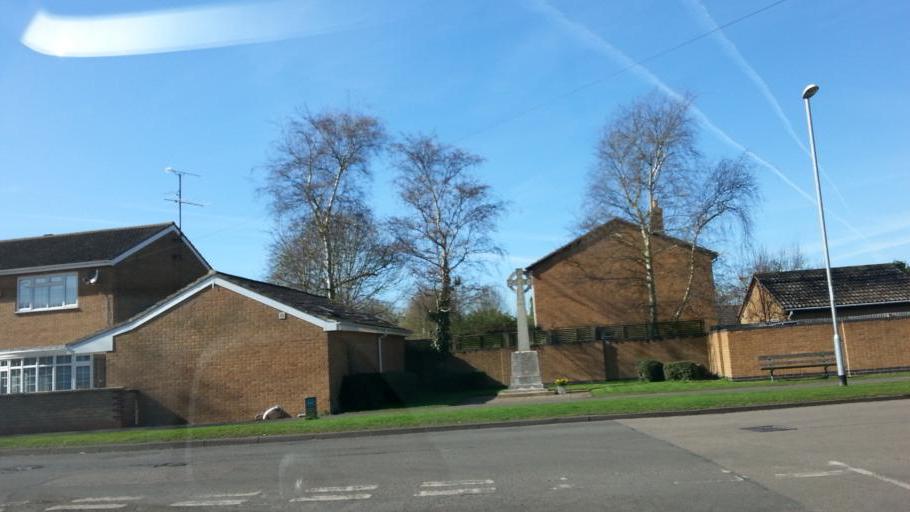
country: GB
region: England
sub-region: Cambridgeshire
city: Swavesey
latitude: 52.3128
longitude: 0.0169
